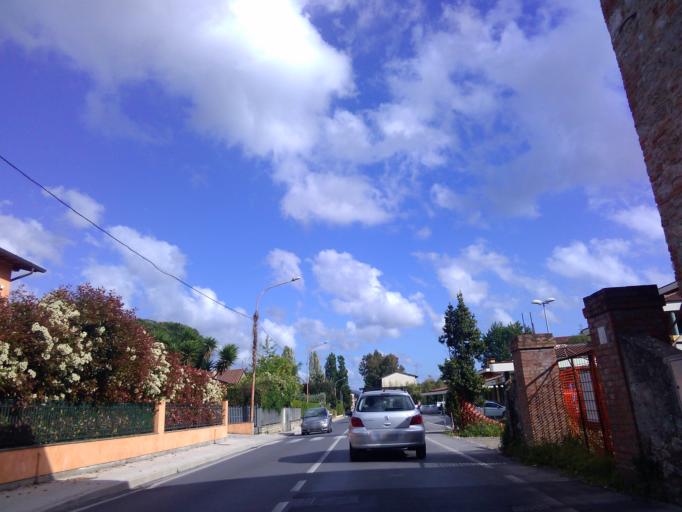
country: IT
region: Tuscany
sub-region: Provincia di Lucca
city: Pietrasanta
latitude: 43.9652
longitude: 10.2224
